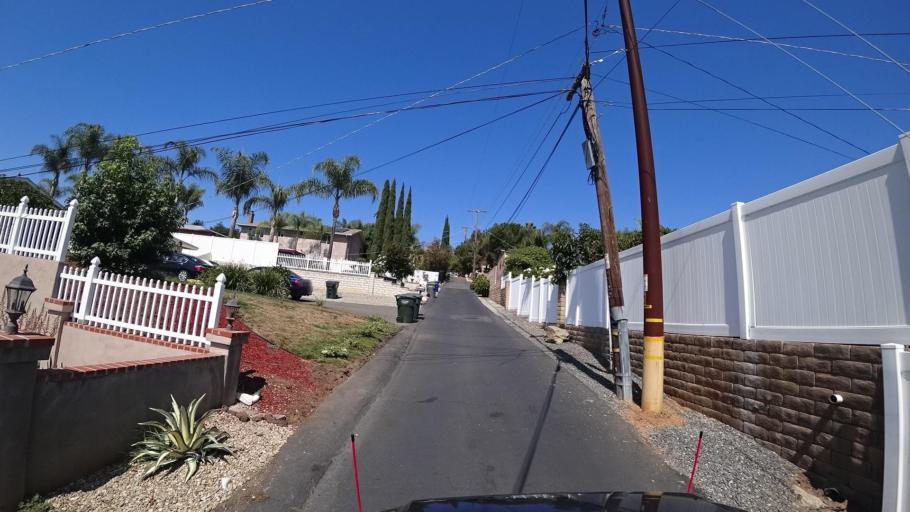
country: US
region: California
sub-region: San Diego County
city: Lake San Marcos
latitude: 33.1628
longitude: -117.2096
